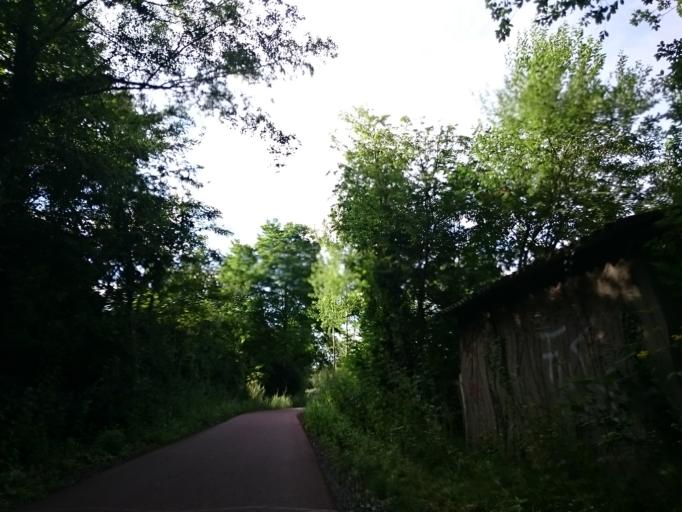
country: FR
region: Lower Normandy
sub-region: Departement du Calvados
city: Saint-Andre-sur-Orne
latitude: 49.1141
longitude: -0.3890
